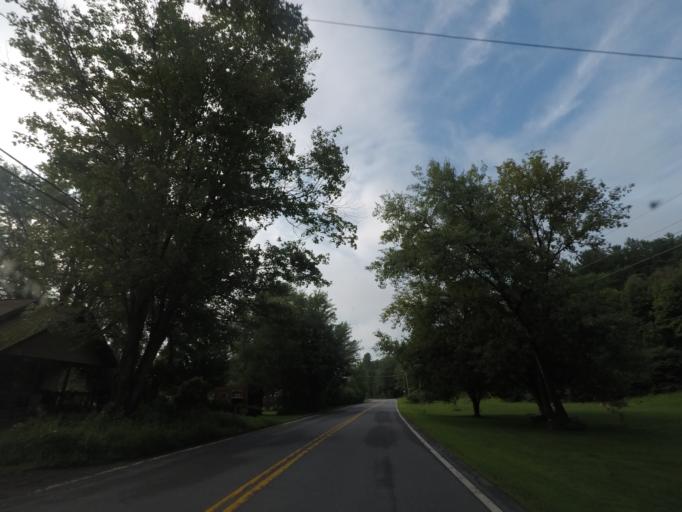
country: US
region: New York
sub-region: Rensselaer County
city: Nassau
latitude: 42.5347
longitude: -73.6084
